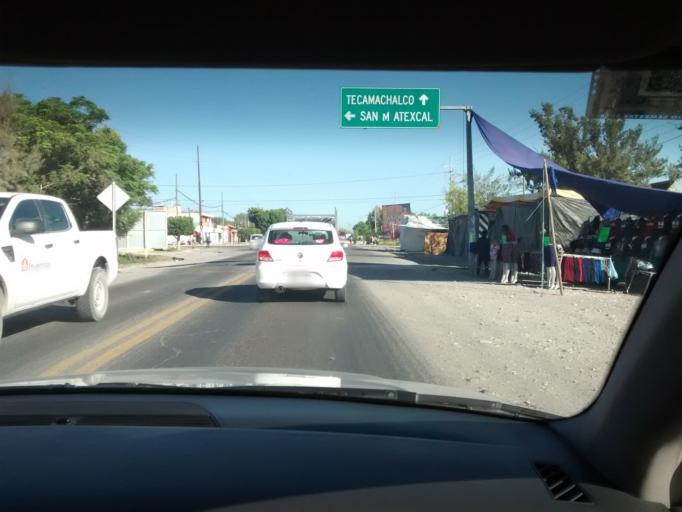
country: MX
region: Puebla
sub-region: Tehuacan
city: Magdalena Cuayucatepec
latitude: 18.5155
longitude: -97.4989
